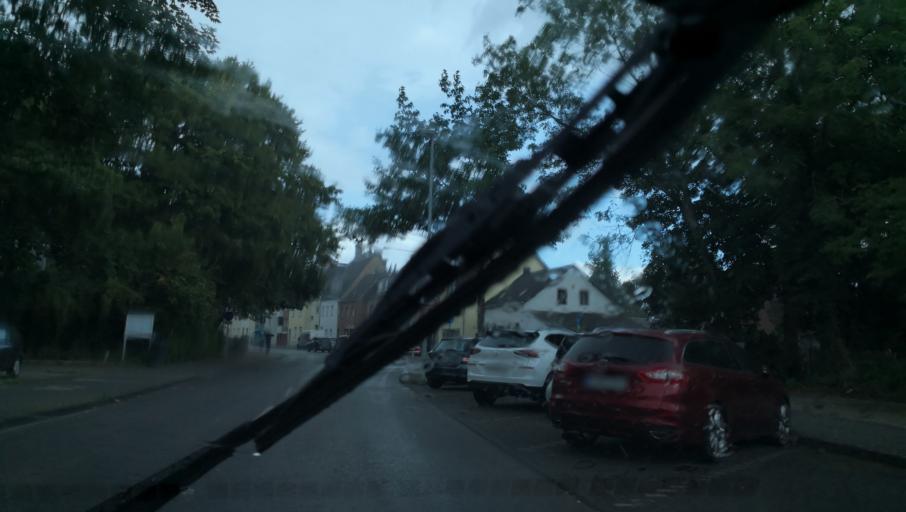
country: DE
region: North Rhine-Westphalia
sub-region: Regierungsbezirk Koln
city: Bilderstoeckchen
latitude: 50.9949
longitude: 6.9083
